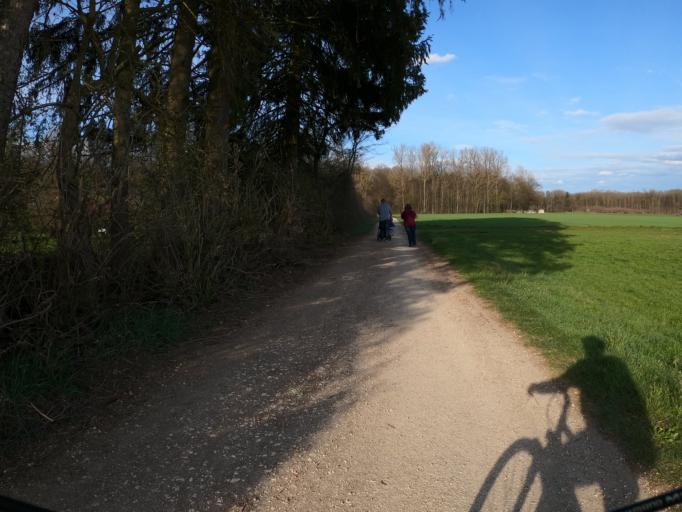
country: DE
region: Bavaria
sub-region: Swabia
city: Holzheim
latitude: 48.4175
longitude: 10.0762
